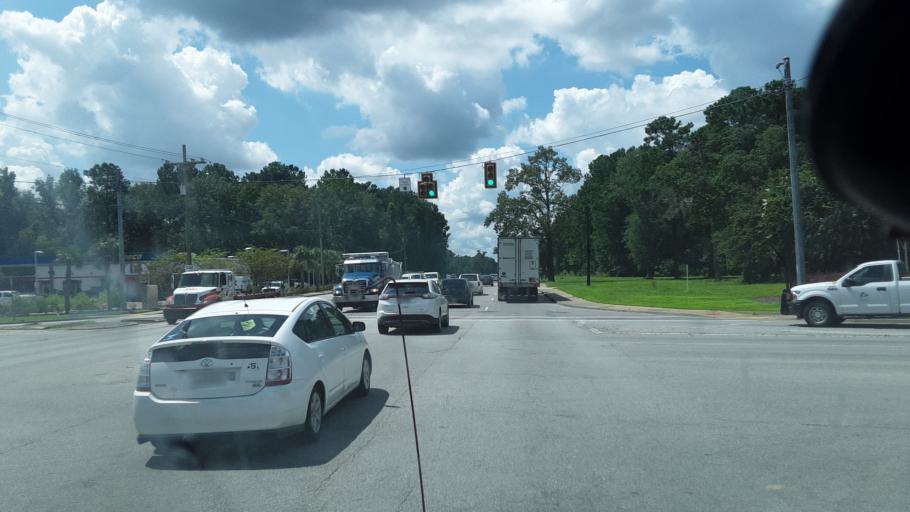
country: US
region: South Carolina
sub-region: Berkeley County
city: Sangaree
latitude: 33.0637
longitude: -80.0934
